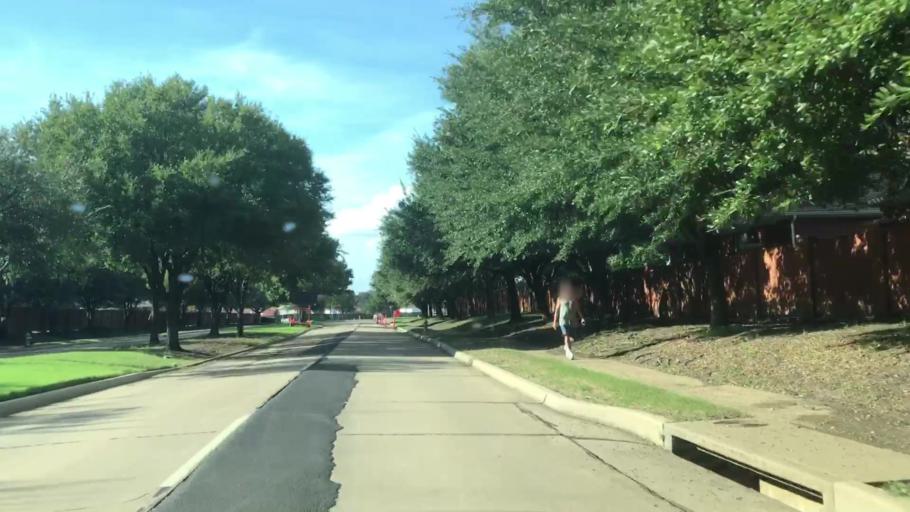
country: US
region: Texas
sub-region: Dallas County
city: Coppell
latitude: 32.9346
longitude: -96.9618
